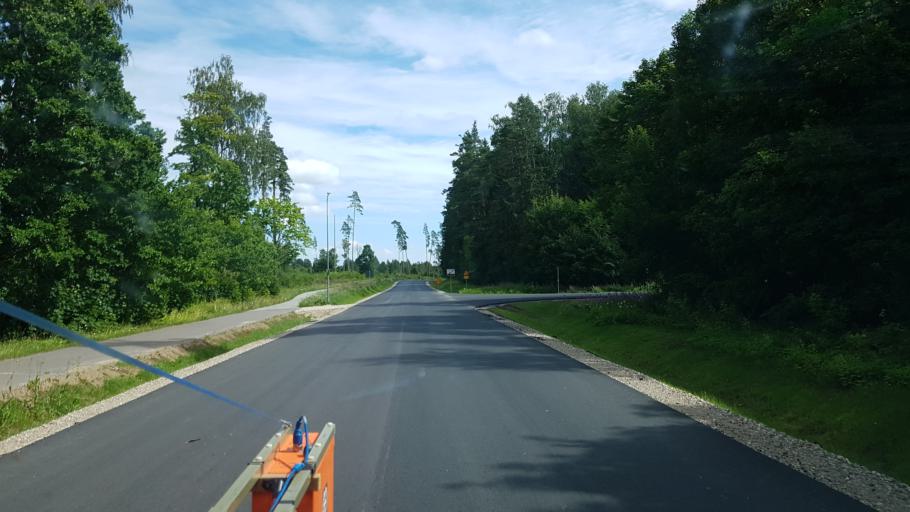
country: EE
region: Viljandimaa
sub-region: Suure-Jaani vald
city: Suure-Jaani
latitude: 58.5386
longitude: 25.5002
